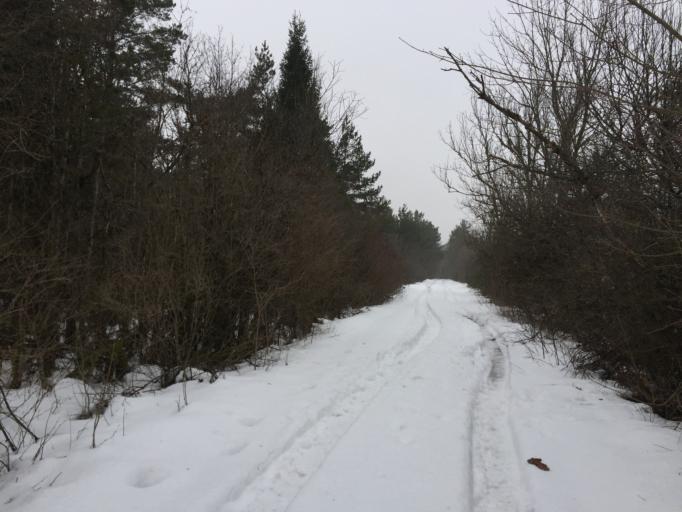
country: EE
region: Saare
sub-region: Orissaare vald
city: Orissaare
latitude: 58.4205
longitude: 22.8196
